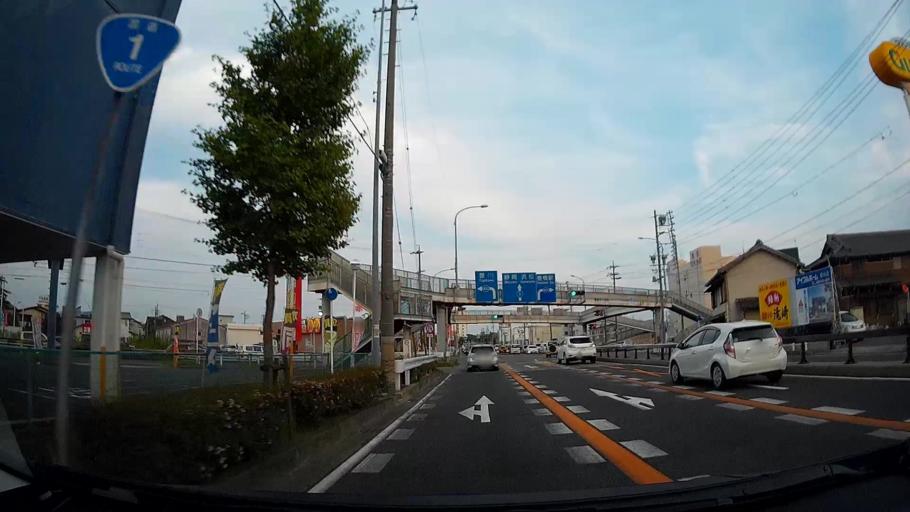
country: JP
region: Aichi
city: Toyohashi
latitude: 34.7768
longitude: 137.3869
